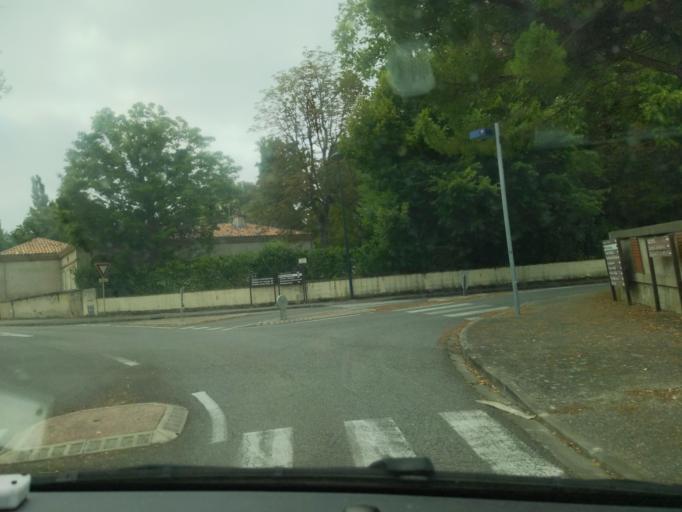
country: FR
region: Midi-Pyrenees
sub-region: Departement de la Haute-Garonne
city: Auzeville-Tolosane
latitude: 43.5257
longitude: 1.4868
